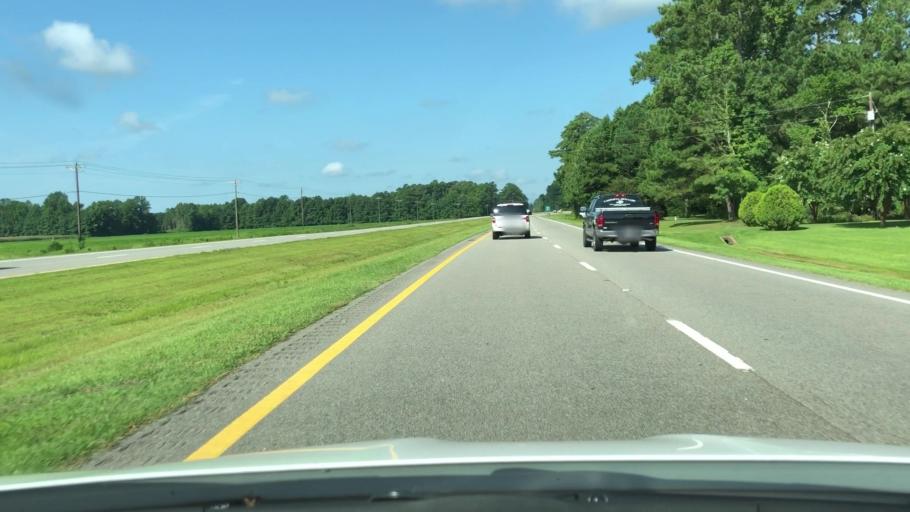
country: US
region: North Carolina
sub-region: Chowan County
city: Edenton
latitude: 36.0942
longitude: -76.5502
